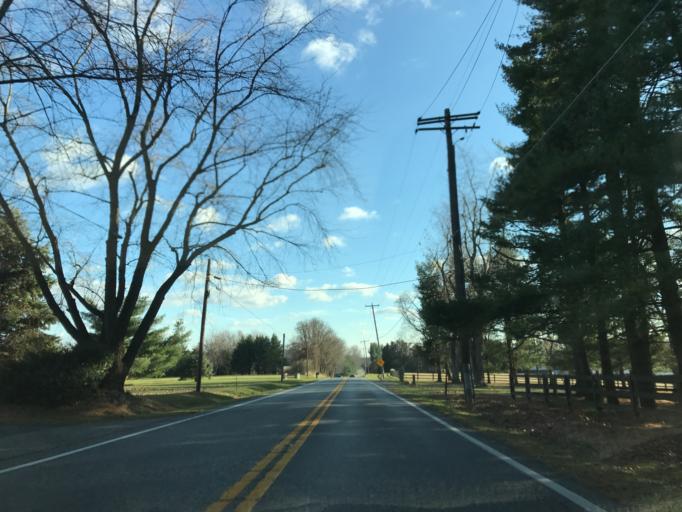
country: US
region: Maryland
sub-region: Harford County
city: Jarrettsville
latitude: 39.6092
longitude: -76.5149
